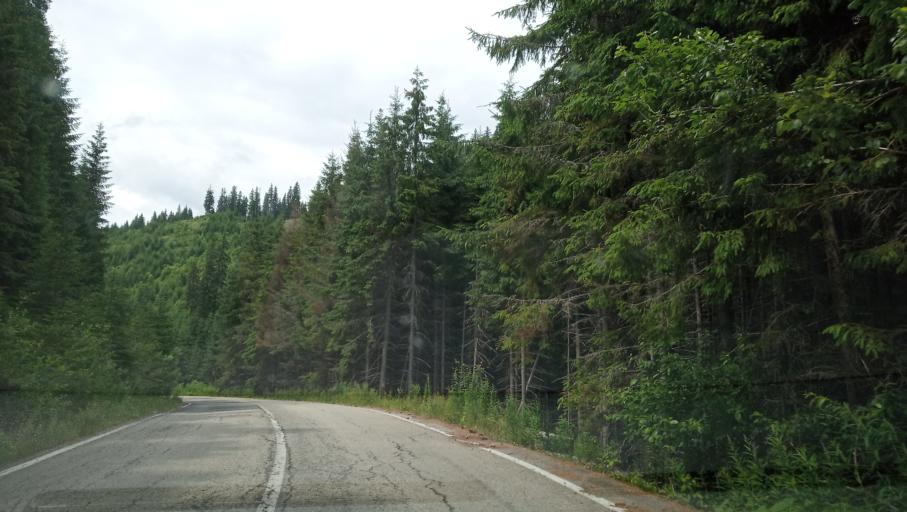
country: RO
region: Valcea
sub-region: Comuna Voineasa
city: Voineasa
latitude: 45.4240
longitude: 23.7496
